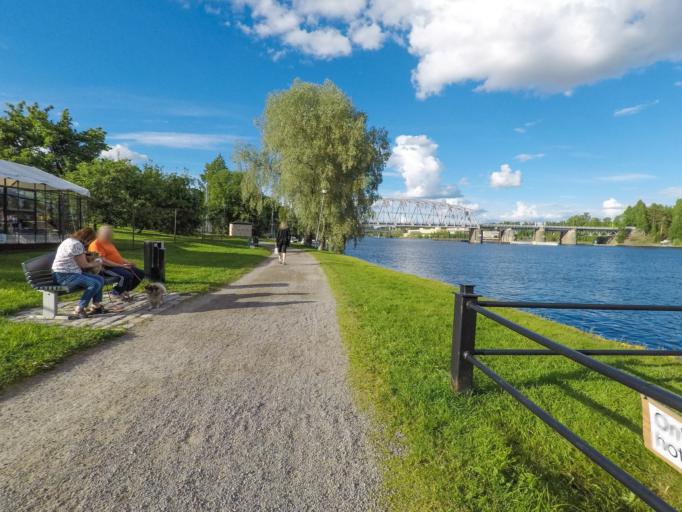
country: FI
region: Southern Savonia
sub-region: Savonlinna
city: Savonlinna
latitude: 61.8656
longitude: 28.8995
